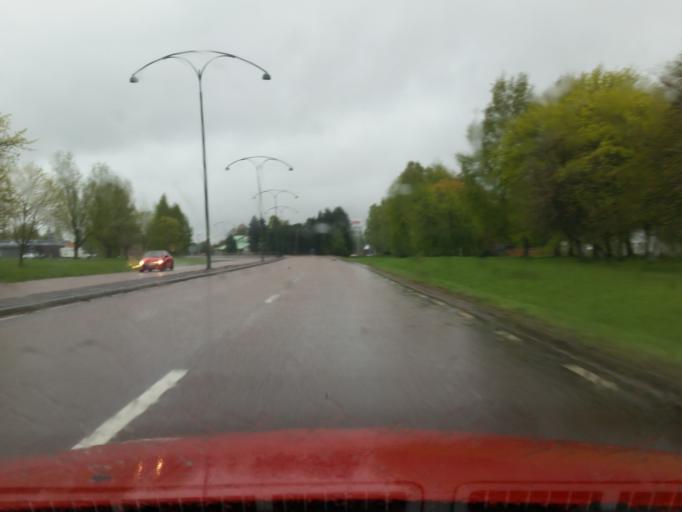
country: SE
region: Dalarna
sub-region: Borlange Kommun
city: Borlaenge
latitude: 60.4787
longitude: 15.4316
